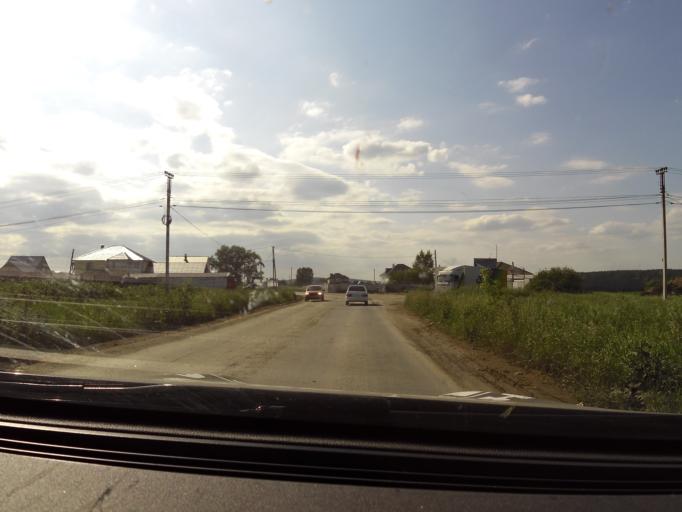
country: RU
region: Sverdlovsk
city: Shirokaya Rechka
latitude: 56.7897
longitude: 60.4810
